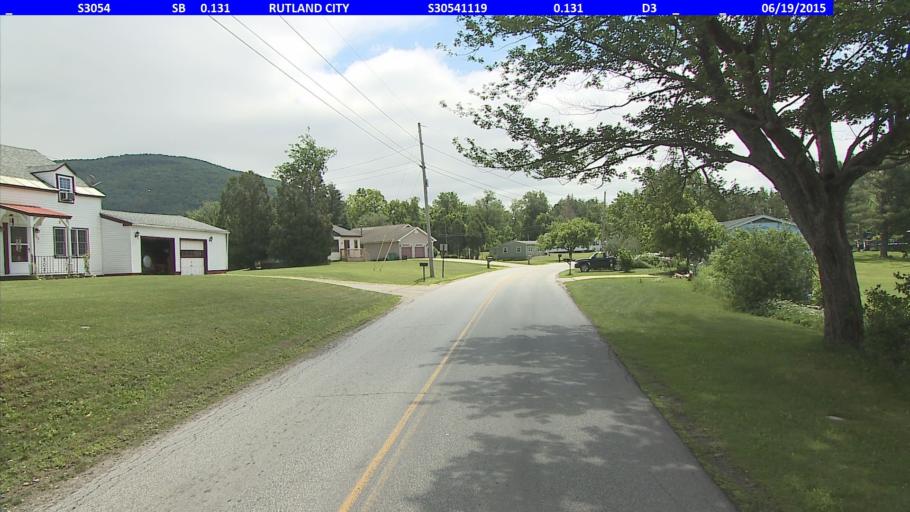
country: US
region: Vermont
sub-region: Rutland County
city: Rutland
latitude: 43.5952
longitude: -72.9500
